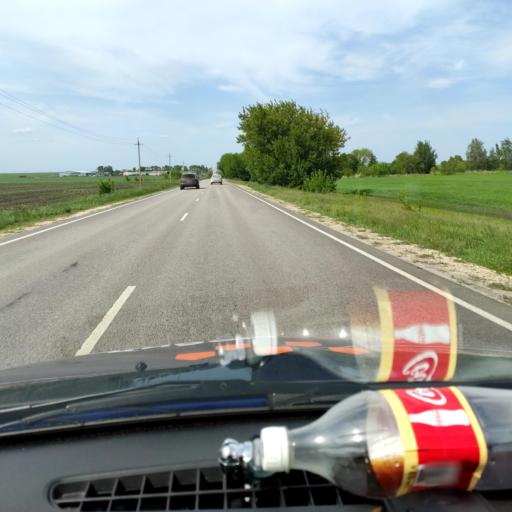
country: RU
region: Voronezj
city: Novaya Usman'
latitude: 51.5698
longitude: 39.3755
